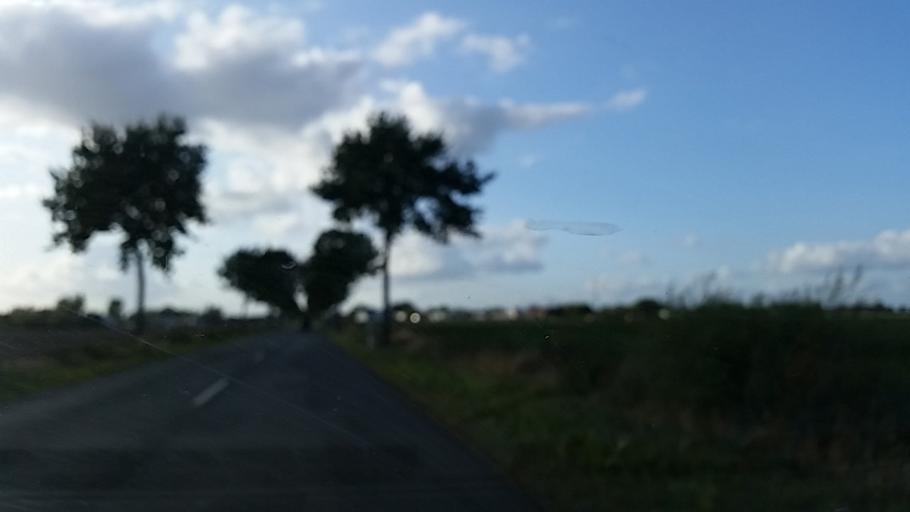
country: DE
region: Lower Saxony
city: Vordorf
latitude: 52.3603
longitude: 10.5317
